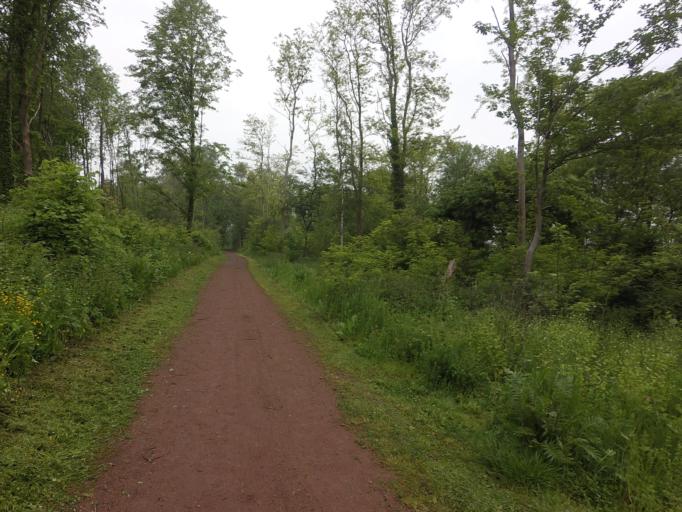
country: NL
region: Limburg
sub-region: Gemeente Kerkrade
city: Kerkrade
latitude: 50.8576
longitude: 6.0498
